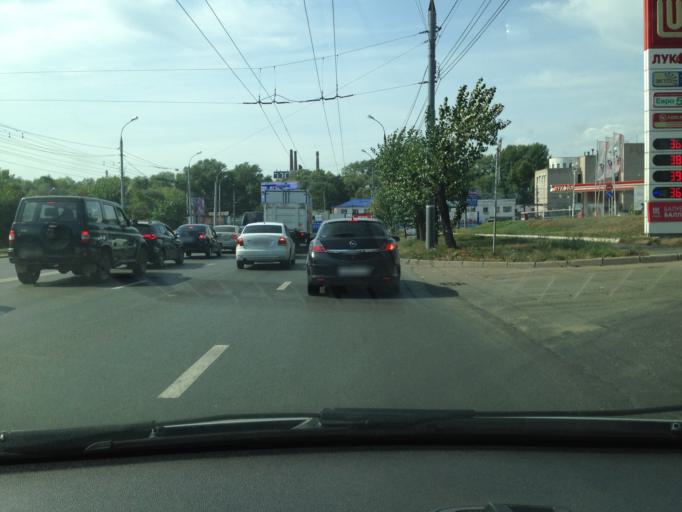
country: RU
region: Udmurtiya
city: Izhevsk
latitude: 56.8373
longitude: 53.2038
